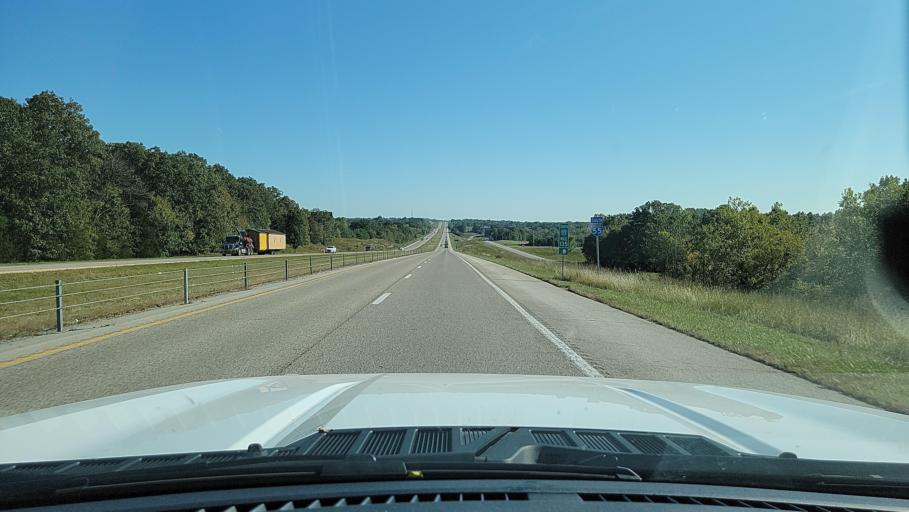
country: US
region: Missouri
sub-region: Perry County
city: Perryville
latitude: 37.7775
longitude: -89.9346
